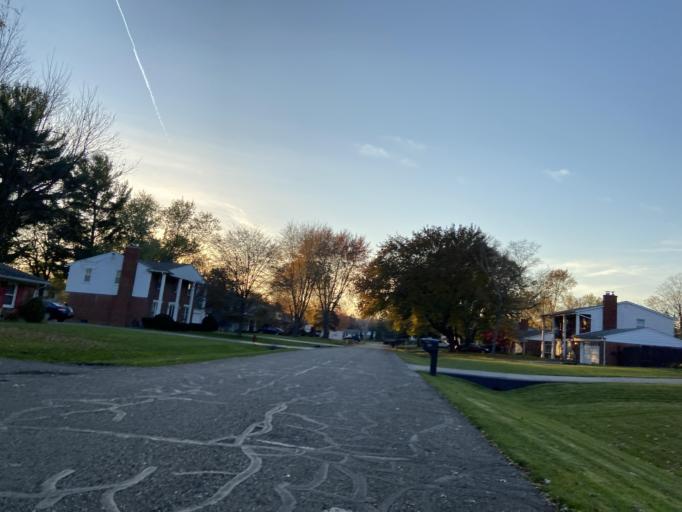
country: US
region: Michigan
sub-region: Oakland County
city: Farmington Hills
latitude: 42.5043
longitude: -83.3670
